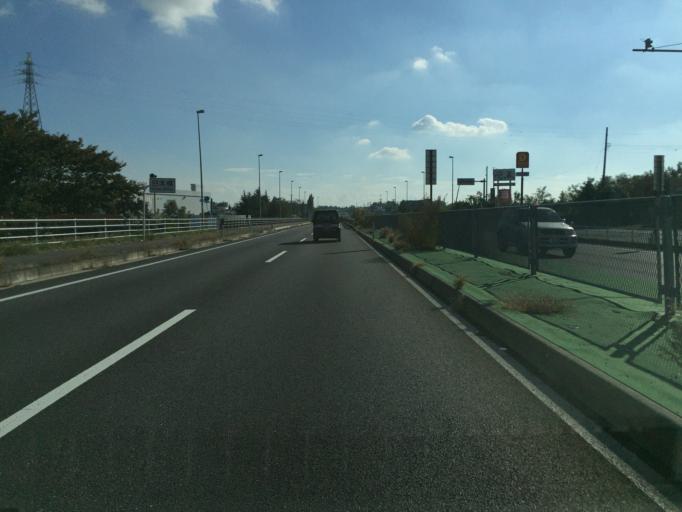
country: JP
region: Fukushima
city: Motomiya
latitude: 37.4781
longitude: 140.3790
